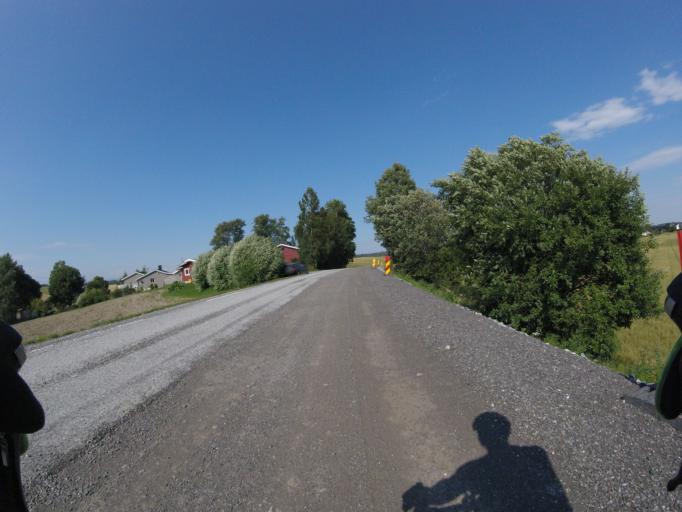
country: NO
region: Akershus
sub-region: Ullensaker
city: Klofta
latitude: 60.0941
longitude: 11.1608
